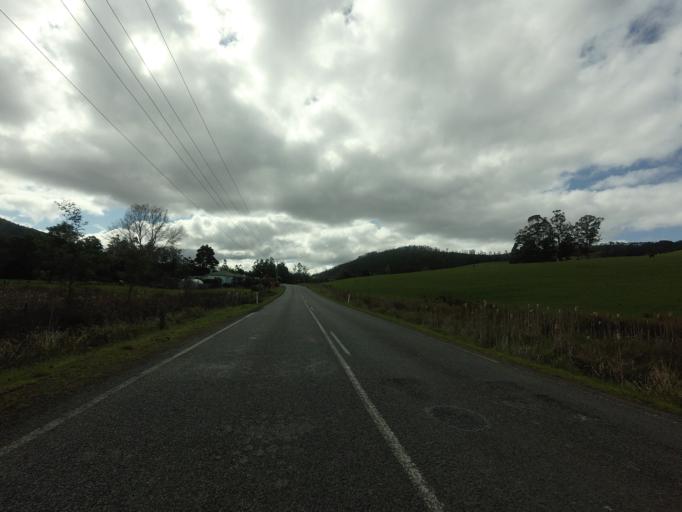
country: AU
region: Tasmania
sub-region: Huon Valley
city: Cygnet
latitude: -43.2902
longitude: 147.0109
